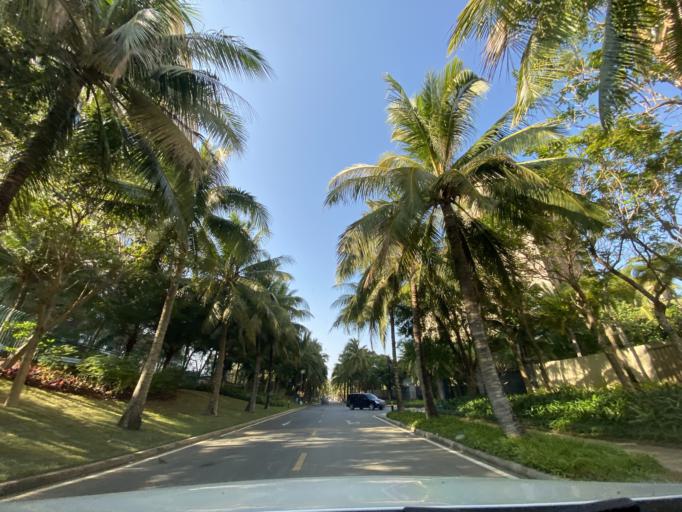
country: CN
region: Hainan
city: Yingzhou
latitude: 18.4162
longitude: 109.8969
